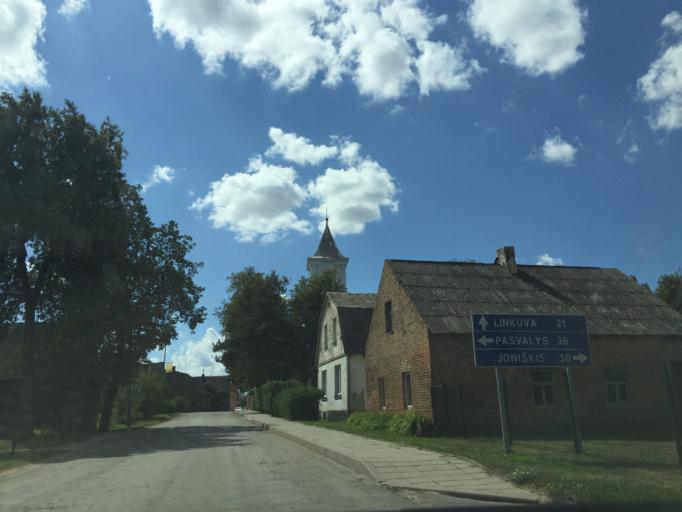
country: LV
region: Rundales
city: Pilsrundale
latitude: 56.2741
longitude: 24.0000
